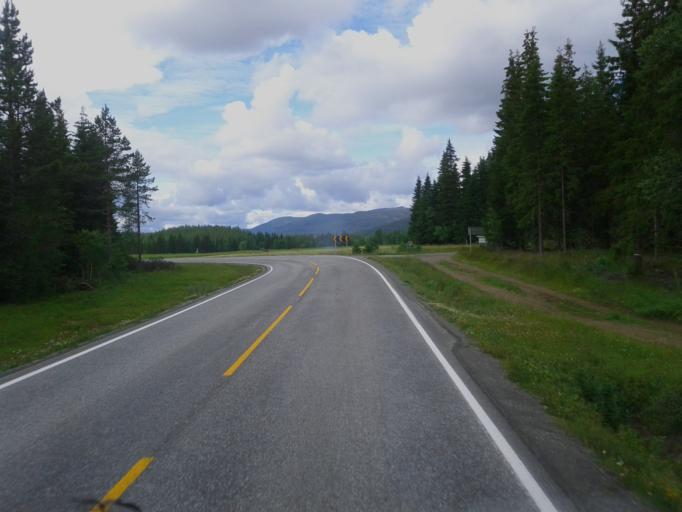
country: NO
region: Nord-Trondelag
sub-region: Hoylandet
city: Hoylandet
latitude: 64.6615
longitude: 12.6521
